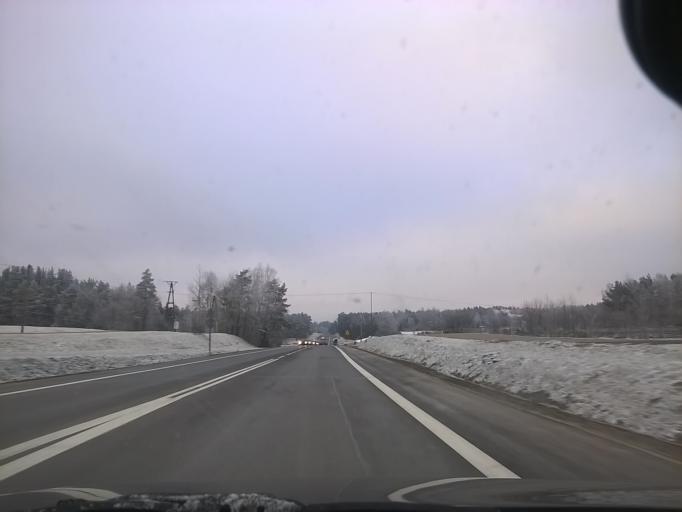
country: PL
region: Warmian-Masurian Voivodeship
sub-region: Powiat olsztynski
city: Barczewo
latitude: 53.7944
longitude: 20.6098
